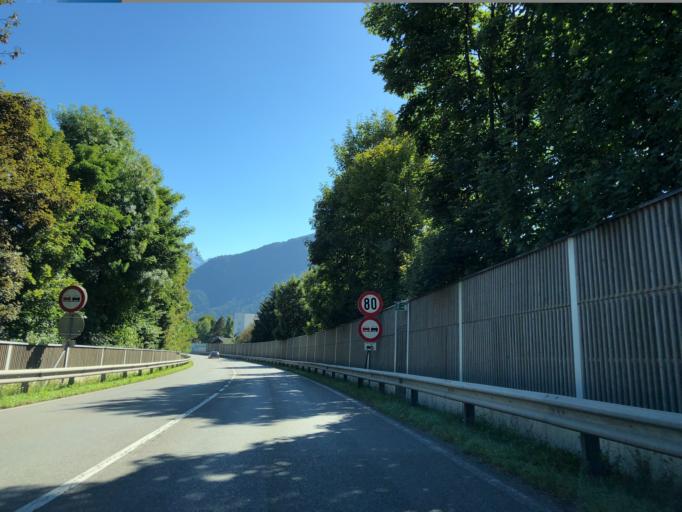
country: AT
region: Tyrol
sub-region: Politischer Bezirk Imst
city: Imst
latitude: 47.2418
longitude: 10.7430
